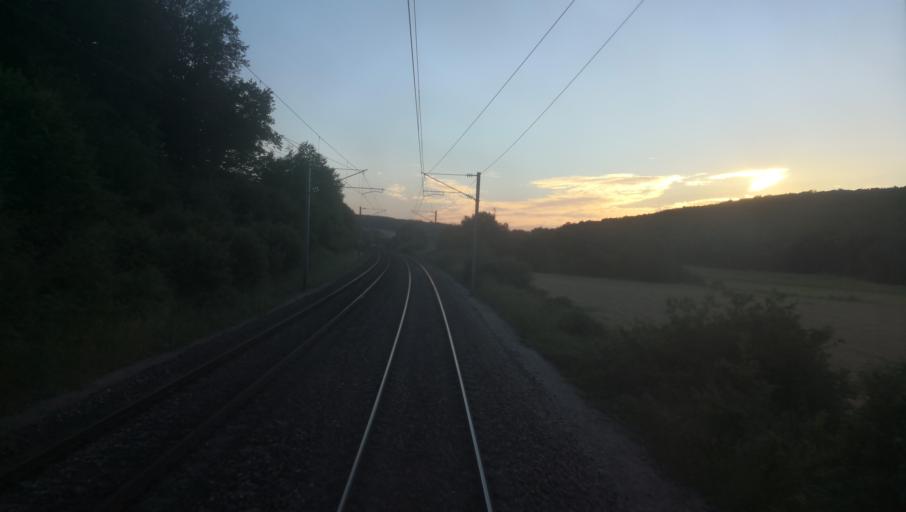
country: FR
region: Haute-Normandie
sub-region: Departement de l'Eure
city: Pacy-sur-Eure
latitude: 48.9757
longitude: 1.3487
